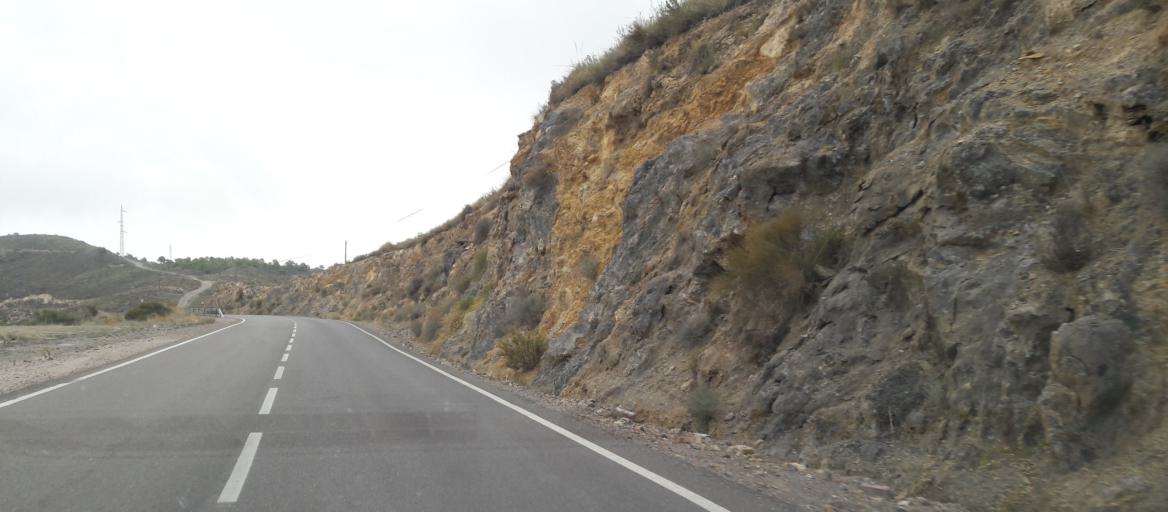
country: ES
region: Andalusia
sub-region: Provincia de Almeria
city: Enix
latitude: 36.8736
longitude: -2.6214
